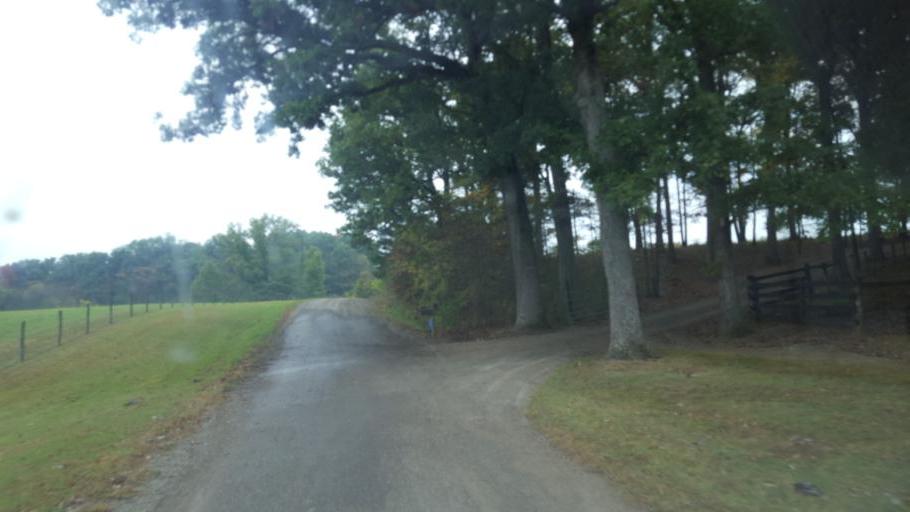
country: US
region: Ohio
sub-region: Ashland County
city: Loudonville
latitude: 40.5744
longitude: -82.2760
